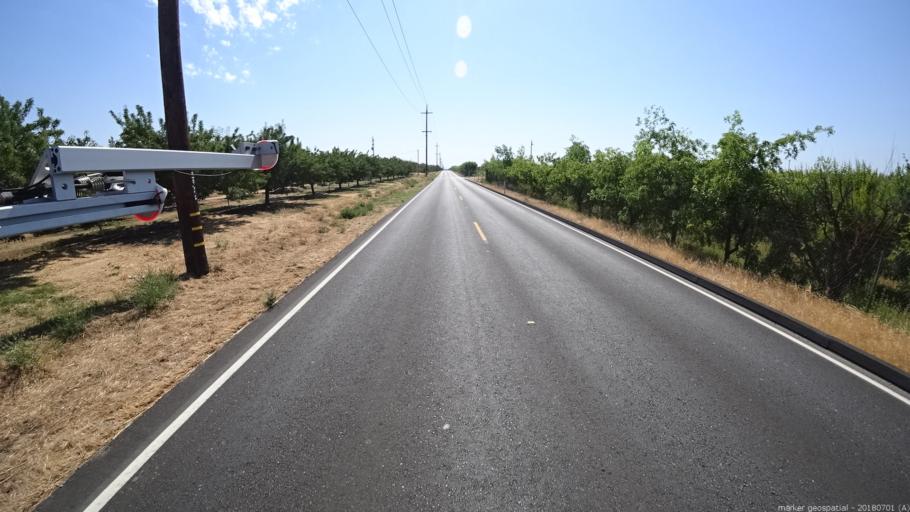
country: US
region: California
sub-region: Madera County
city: Bonadelle Ranchos-Madera Ranchos
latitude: 36.8804
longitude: -119.8717
